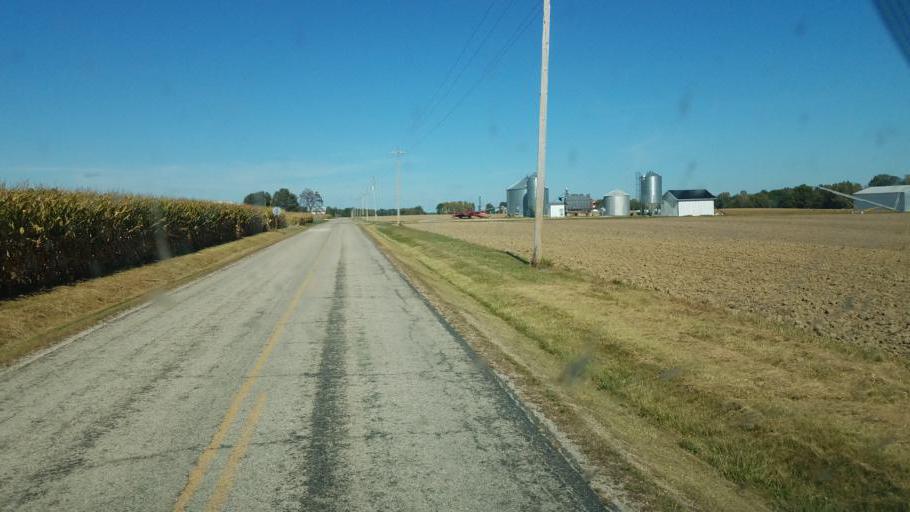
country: US
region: Ohio
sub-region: Huron County
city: Willard
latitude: 40.9735
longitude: -82.7908
